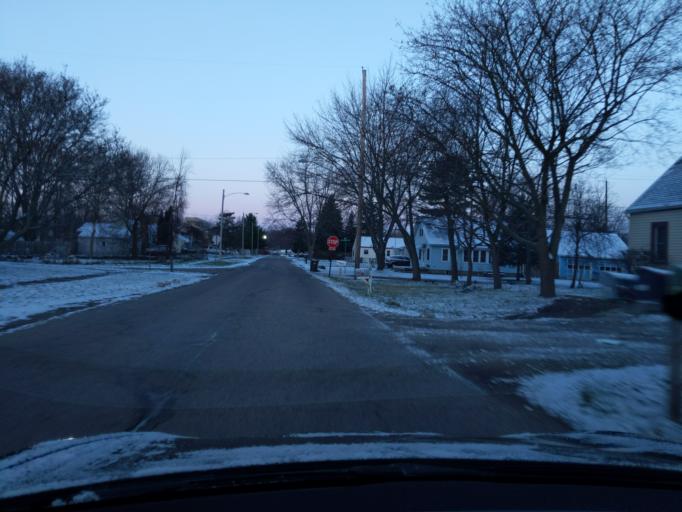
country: US
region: Michigan
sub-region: Ingham County
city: Lansing
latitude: 42.7025
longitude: -84.5644
